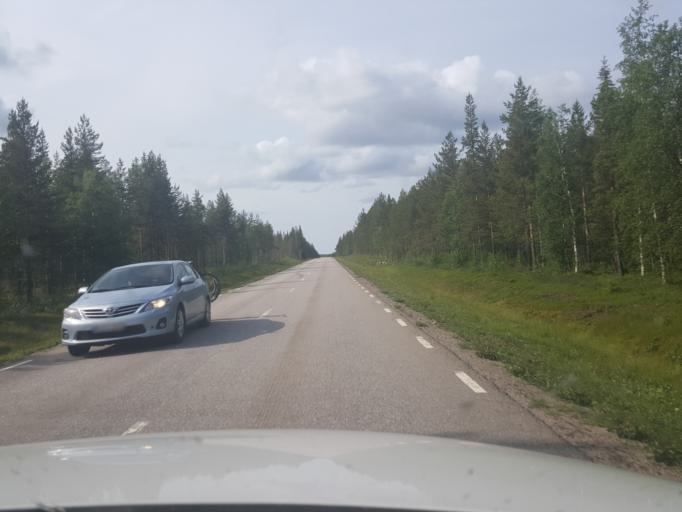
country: SE
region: Norrbotten
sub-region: Arjeplogs Kommun
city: Arjeplog
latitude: 65.6516
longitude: 18.0919
